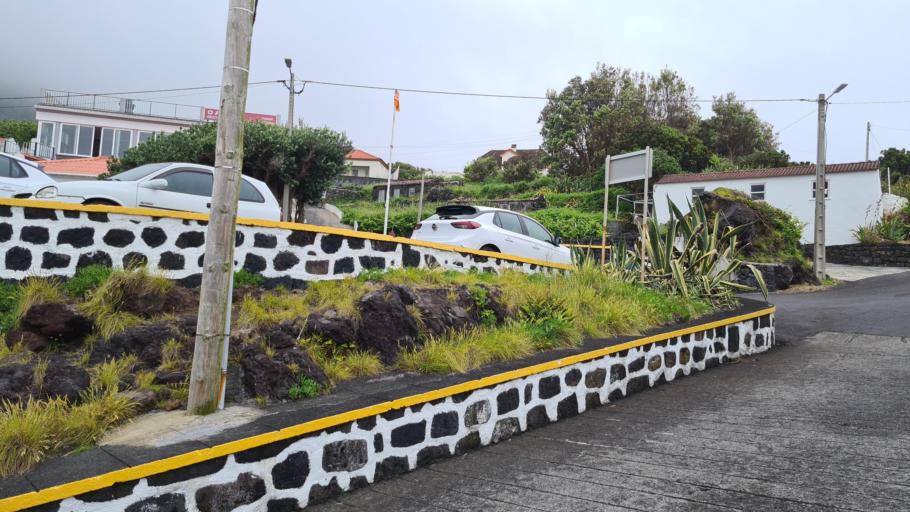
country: PT
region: Azores
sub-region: Sao Roque do Pico
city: Sao Roque do Pico
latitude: 38.6787
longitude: -28.0504
